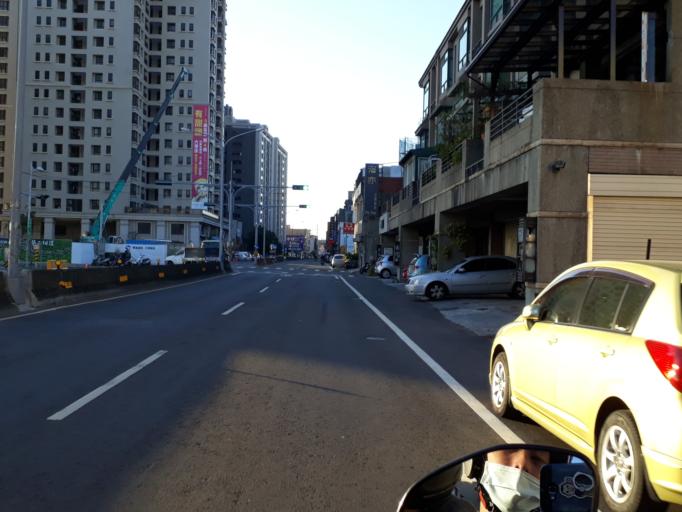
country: TW
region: Taiwan
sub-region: Hsinchu
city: Zhubei
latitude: 24.8259
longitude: 121.0058
